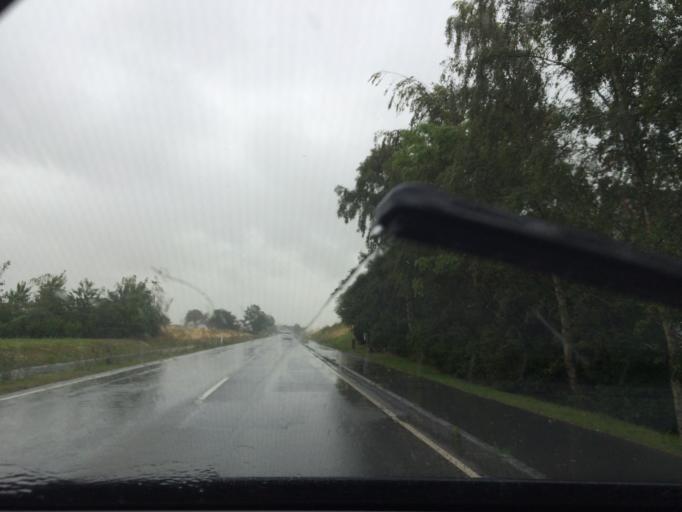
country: DK
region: Zealand
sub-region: Vordingborg Kommune
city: Stege
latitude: 54.9948
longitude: 12.3187
